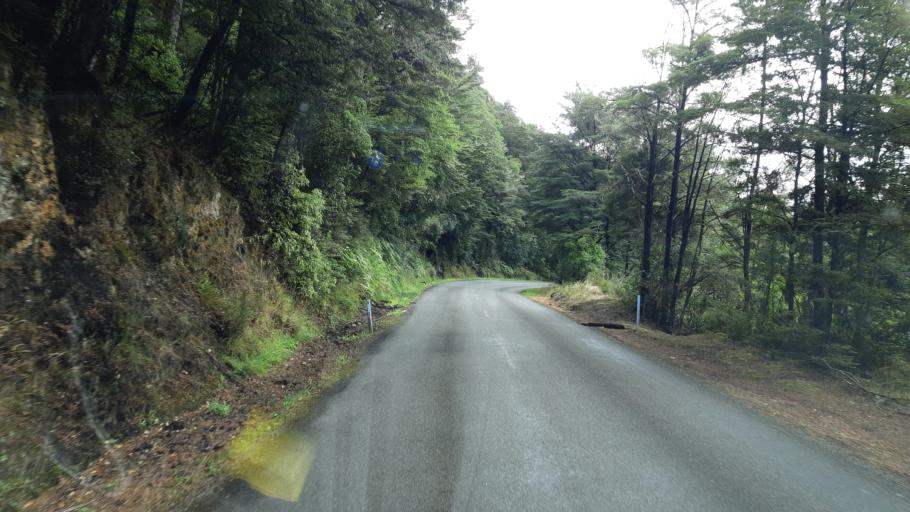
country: NZ
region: West Coast
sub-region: Buller District
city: Westport
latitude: -41.7864
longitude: 172.3676
